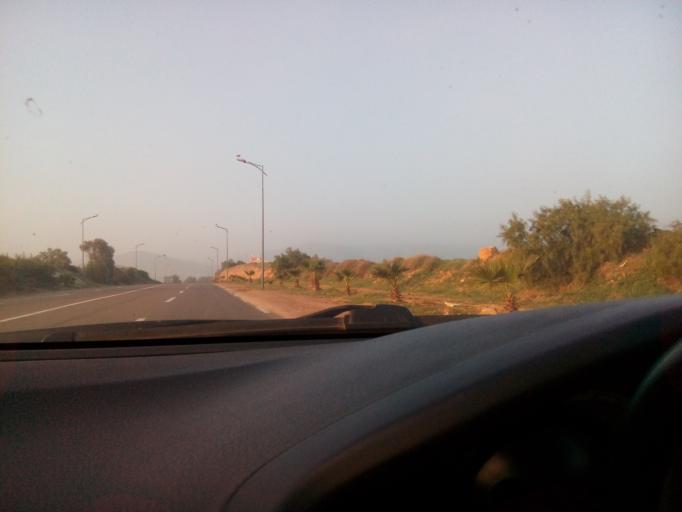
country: DZ
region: Oran
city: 'Ain el Turk
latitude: 35.7123
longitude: -0.8694
